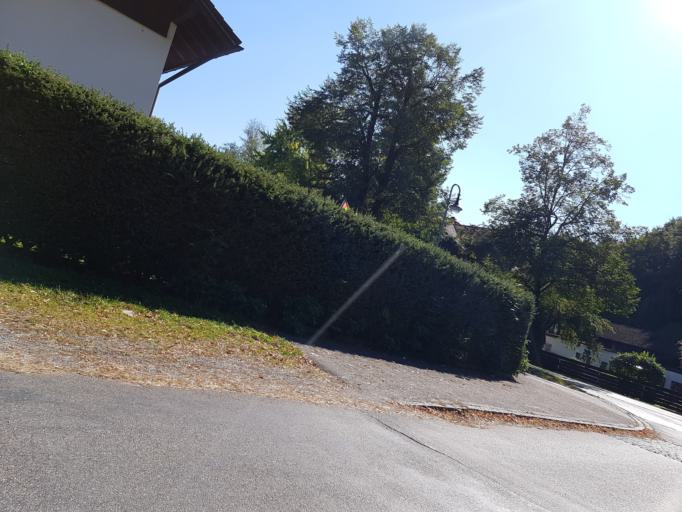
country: DE
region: Bavaria
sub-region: Swabia
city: Fuessen
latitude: 47.5685
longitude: 10.6864
